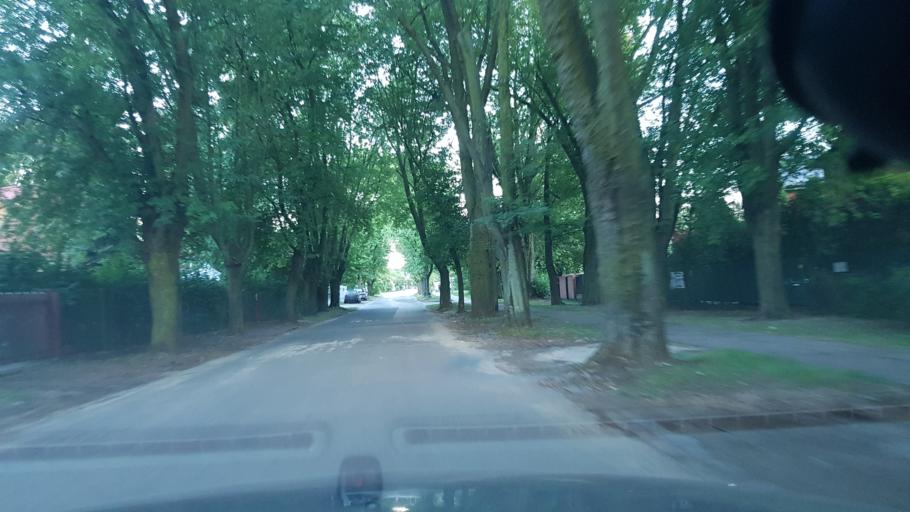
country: PL
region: Masovian Voivodeship
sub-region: Powiat otwocki
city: Jozefow
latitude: 52.1654
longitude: 21.2136
